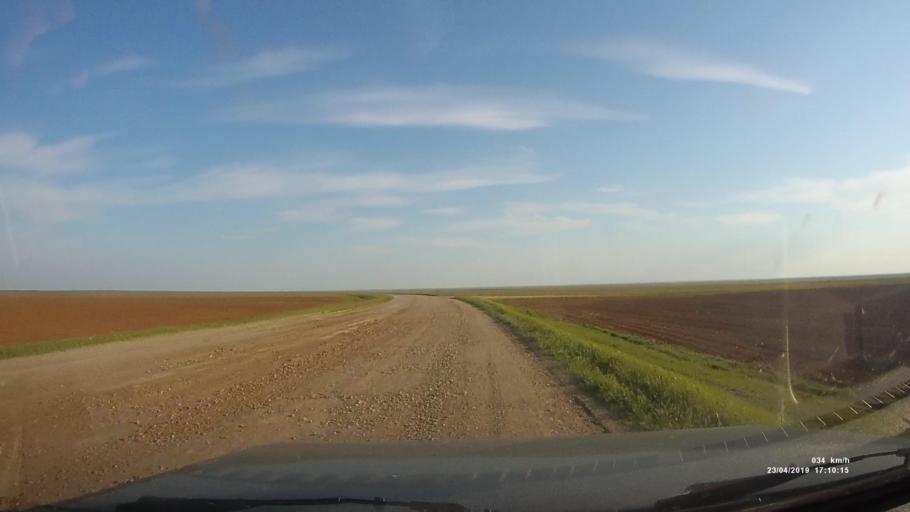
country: RU
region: Kalmykiya
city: Priyutnoye
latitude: 46.2477
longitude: 43.4841
